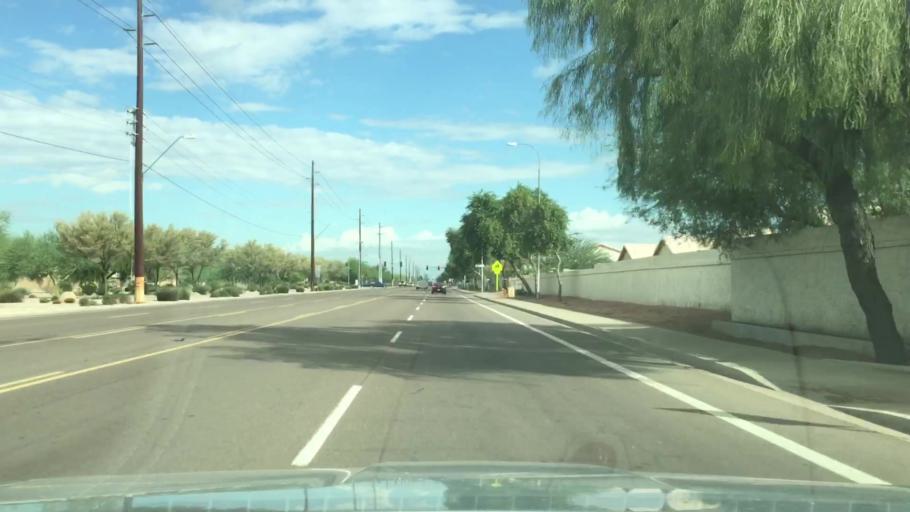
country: US
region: Arizona
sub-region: Maricopa County
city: Tolleson
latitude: 33.4700
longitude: -112.2552
